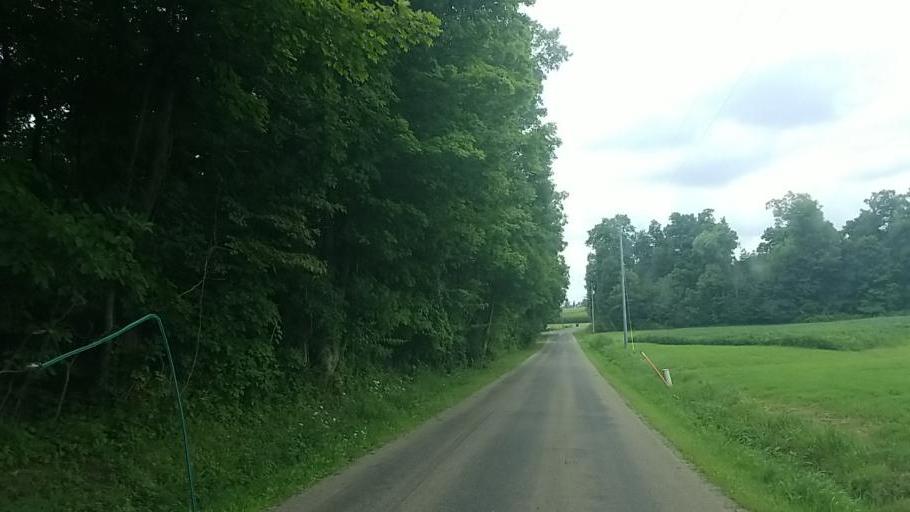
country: US
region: Ohio
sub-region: Knox County
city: Gambier
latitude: 40.3315
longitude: -82.4306
